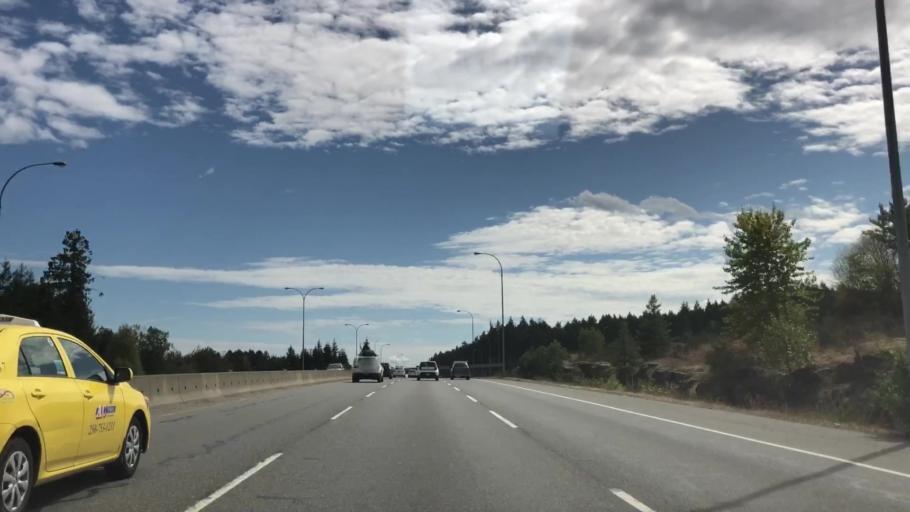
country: CA
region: British Columbia
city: Nanaimo
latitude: 49.1129
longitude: -123.9050
